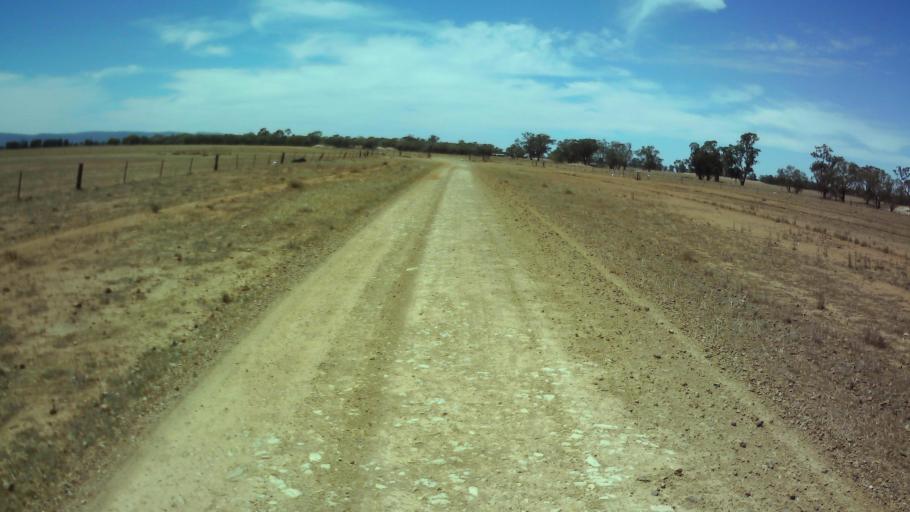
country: AU
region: New South Wales
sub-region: Weddin
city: Grenfell
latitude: -33.8651
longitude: 147.7623
